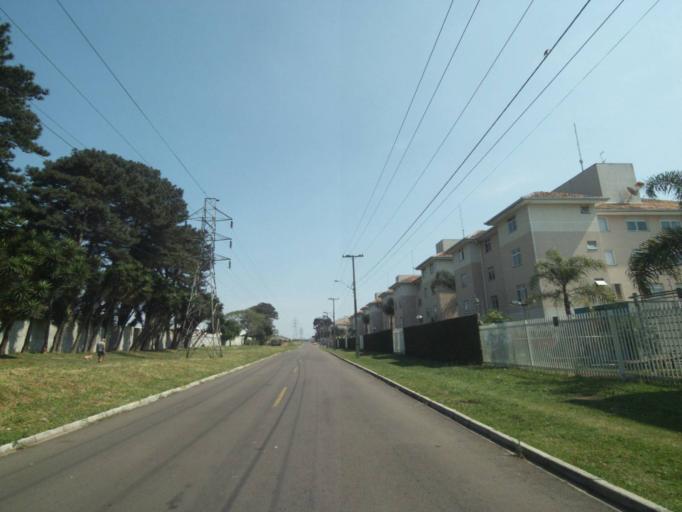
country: BR
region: Parana
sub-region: Curitiba
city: Curitiba
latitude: -25.4835
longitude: -49.3214
